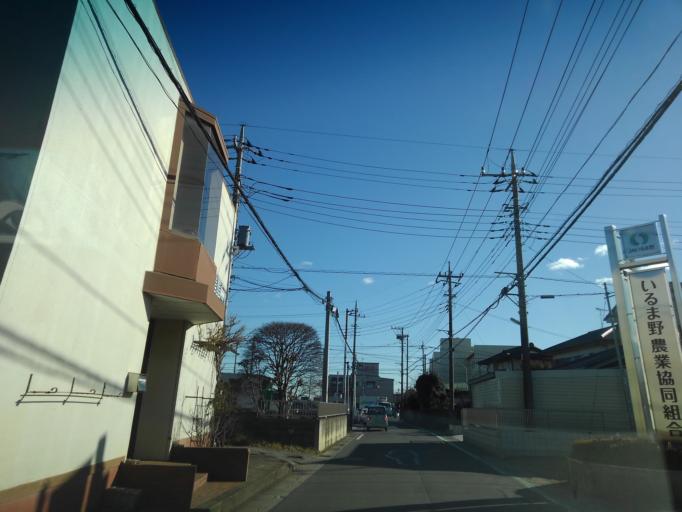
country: JP
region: Saitama
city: Oi
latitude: 35.8063
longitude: 139.5206
